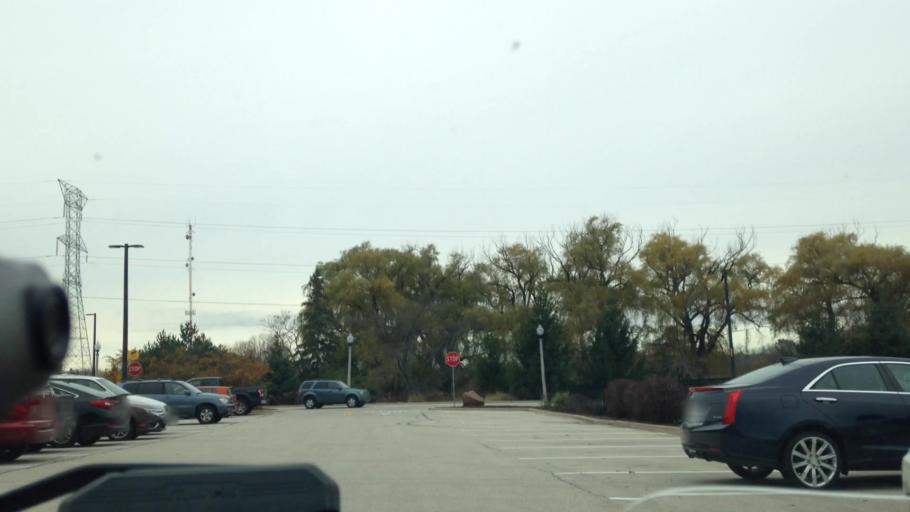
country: US
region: Wisconsin
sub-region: Waukesha County
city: Menomonee Falls
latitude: 43.1974
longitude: -88.1455
